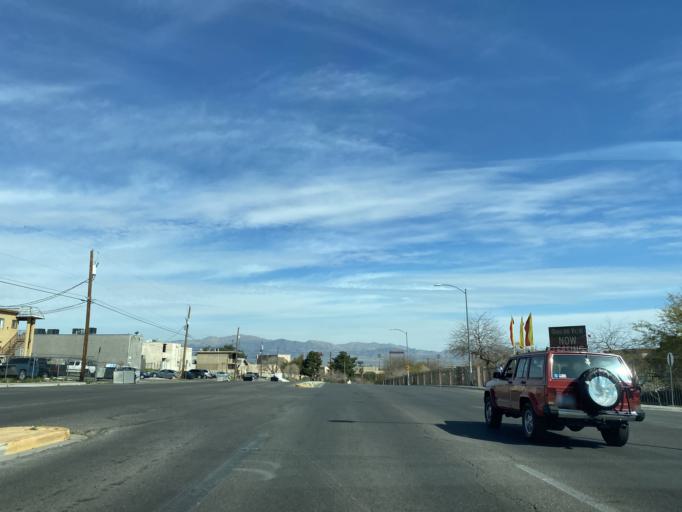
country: US
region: Nevada
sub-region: Clark County
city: Las Vegas
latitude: 36.1755
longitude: -115.1306
